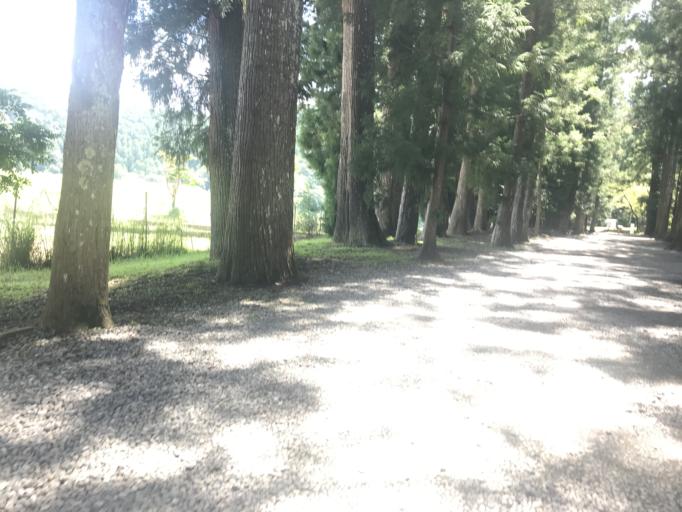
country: JP
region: Wakayama
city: Shingu
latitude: 33.8356
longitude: 135.7755
